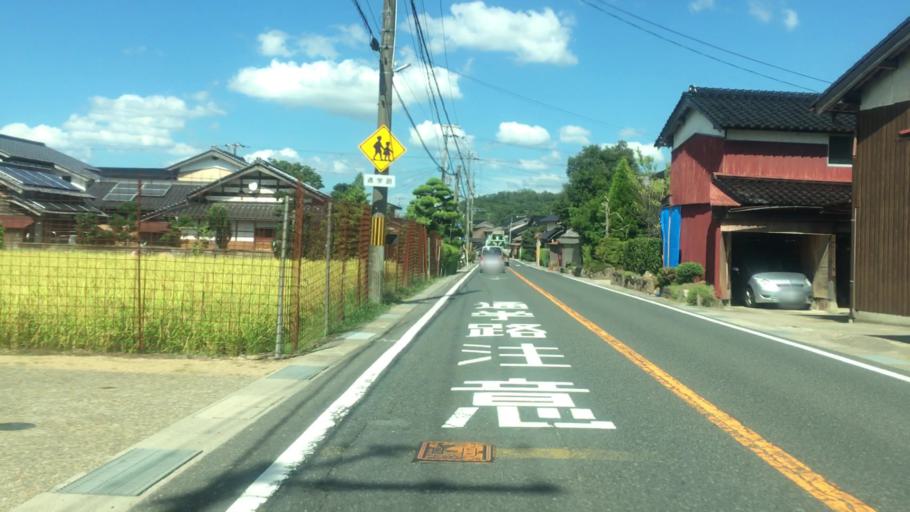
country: JP
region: Kyoto
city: Miyazu
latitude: 35.5904
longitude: 135.0392
